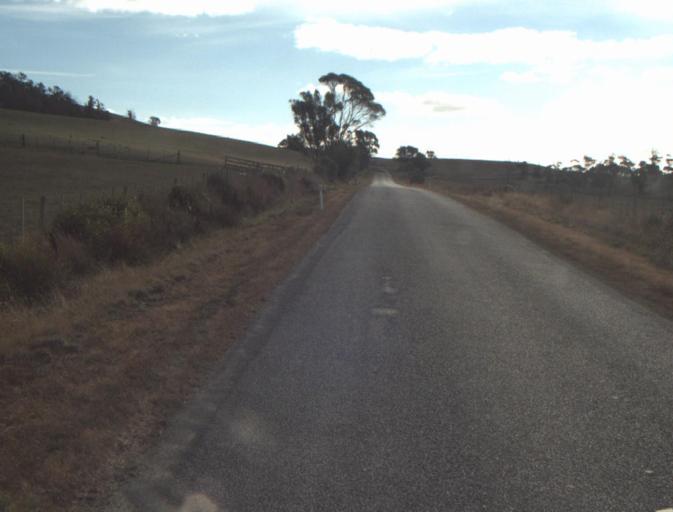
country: AU
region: Tasmania
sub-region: Launceston
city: Mayfield
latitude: -41.2084
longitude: 147.1047
